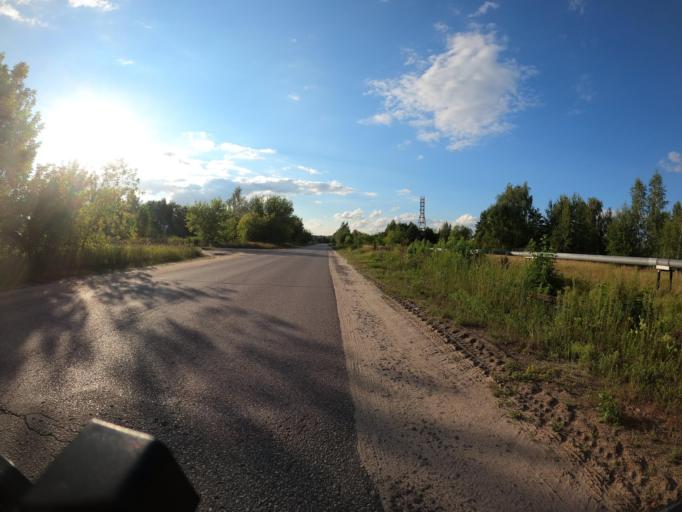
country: RU
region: Moskovskaya
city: Beloozerskiy
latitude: 55.4534
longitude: 38.4875
